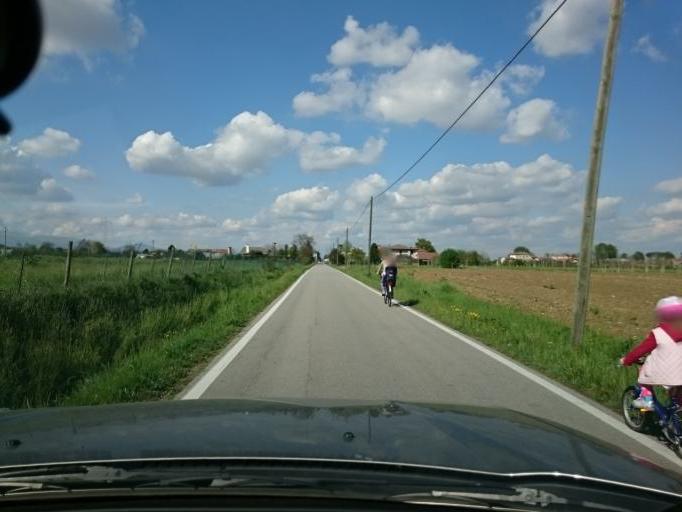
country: IT
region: Veneto
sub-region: Provincia di Padova
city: Villanova
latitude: 45.4837
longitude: 11.9846
